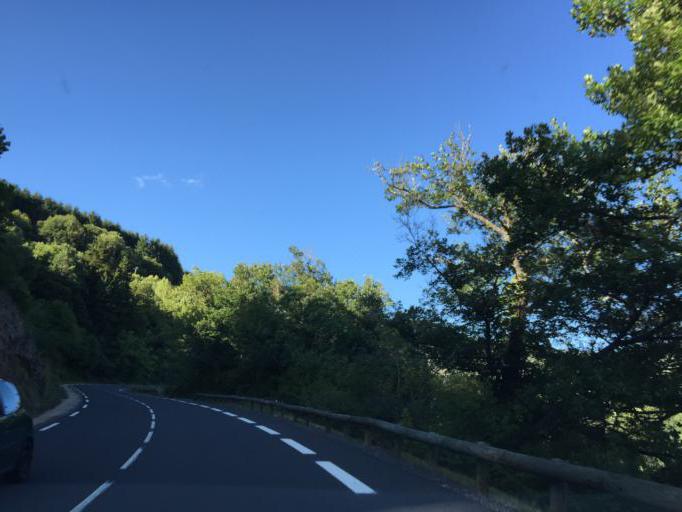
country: FR
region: Auvergne
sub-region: Departement de la Haute-Loire
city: Bains
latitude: 44.9757
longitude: 3.6726
